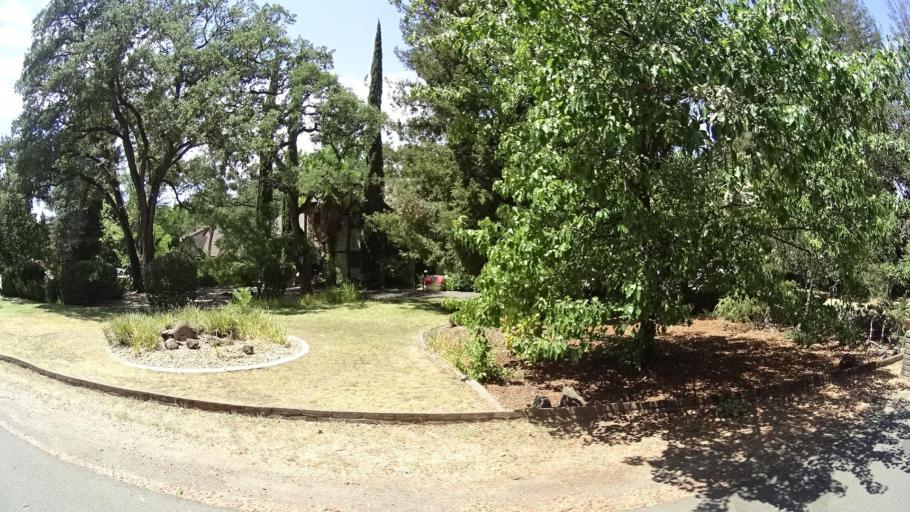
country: US
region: California
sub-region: Placer County
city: Rocklin
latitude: 38.8153
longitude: -121.2348
